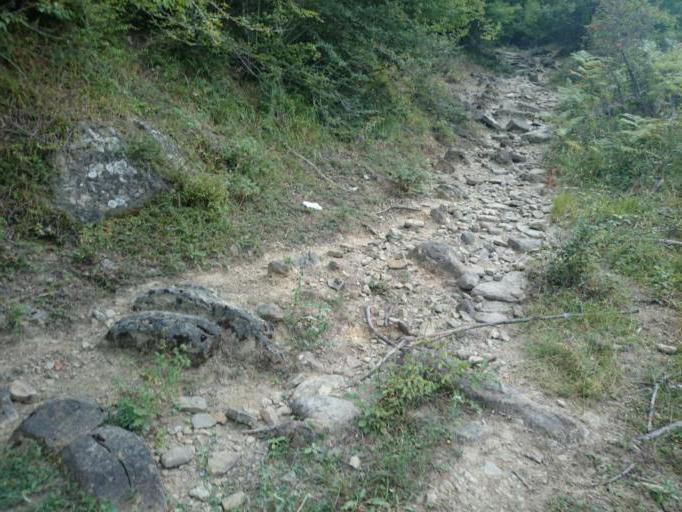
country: AL
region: Elbasan
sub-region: Rrethi i Elbasanit
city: Zavaline
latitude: 40.9542
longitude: 20.2304
